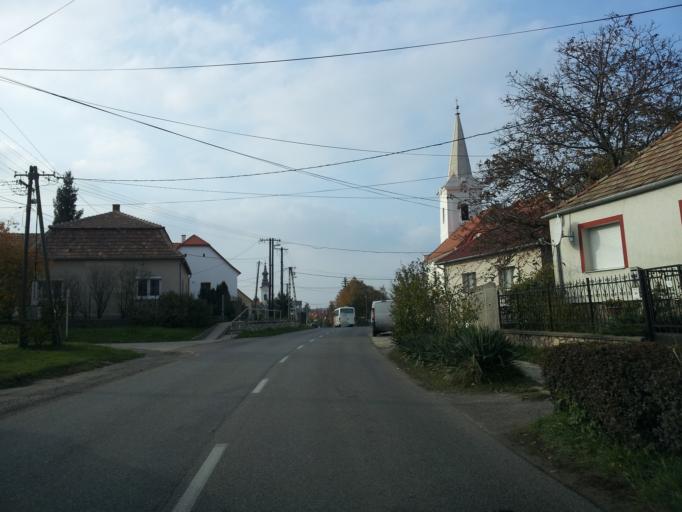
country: HU
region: Komarom-Esztergom
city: Bokod
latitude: 47.4913
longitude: 18.2494
